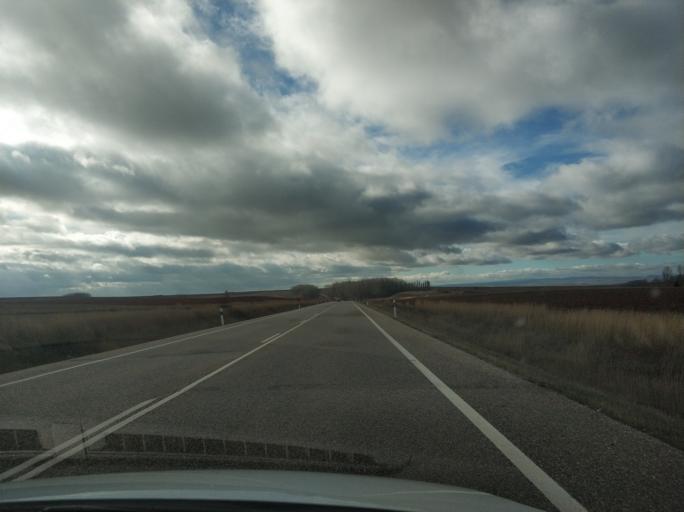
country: ES
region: Castille and Leon
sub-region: Provincia de Segovia
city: Ayllon
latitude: 41.4378
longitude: -3.3470
